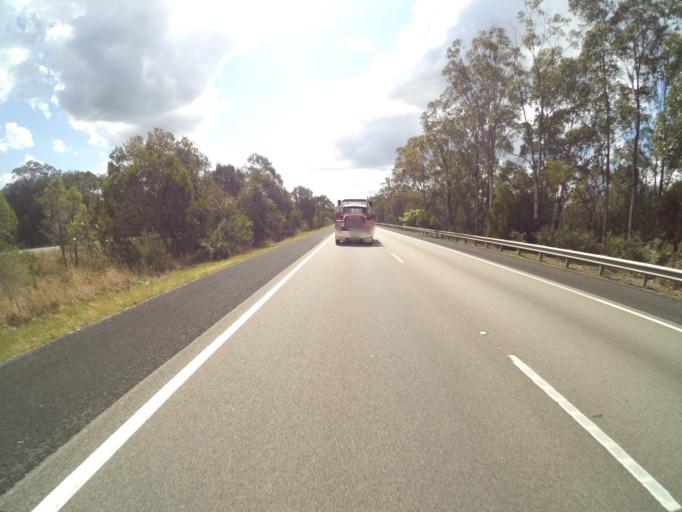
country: AU
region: New South Wales
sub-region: Wollondilly
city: Douglas Park
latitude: -34.2635
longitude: 150.6508
